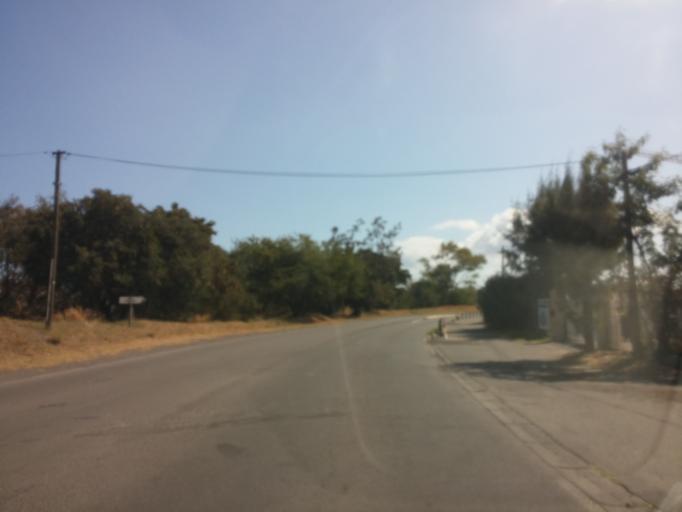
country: RE
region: Reunion
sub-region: Reunion
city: Le Port
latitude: -20.9485
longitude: 55.2830
